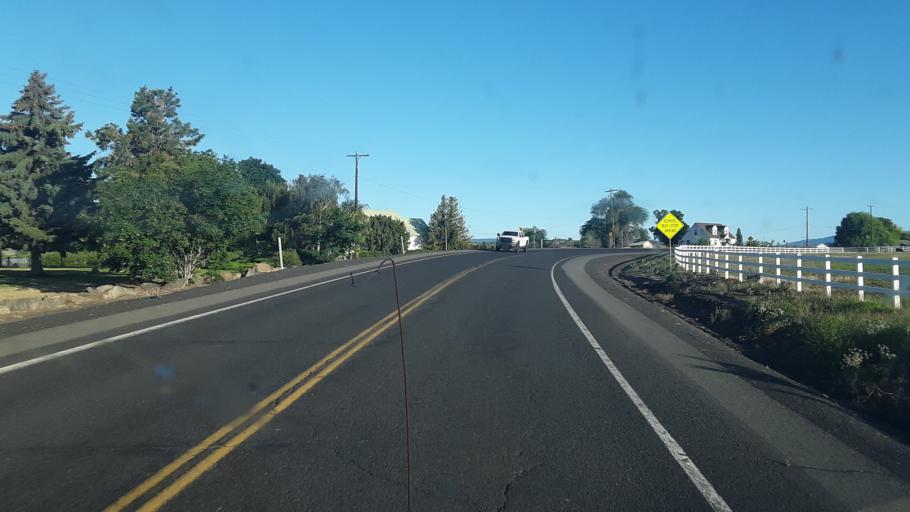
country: US
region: Washington
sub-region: Yakima County
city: Tieton
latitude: 46.6522
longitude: -120.7082
